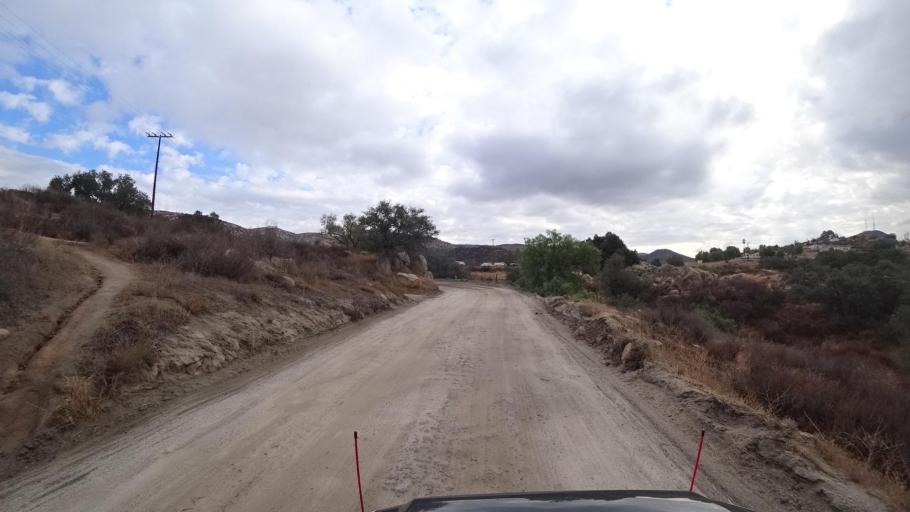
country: MX
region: Baja California
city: Tecate
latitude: 32.5853
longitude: -116.6209
